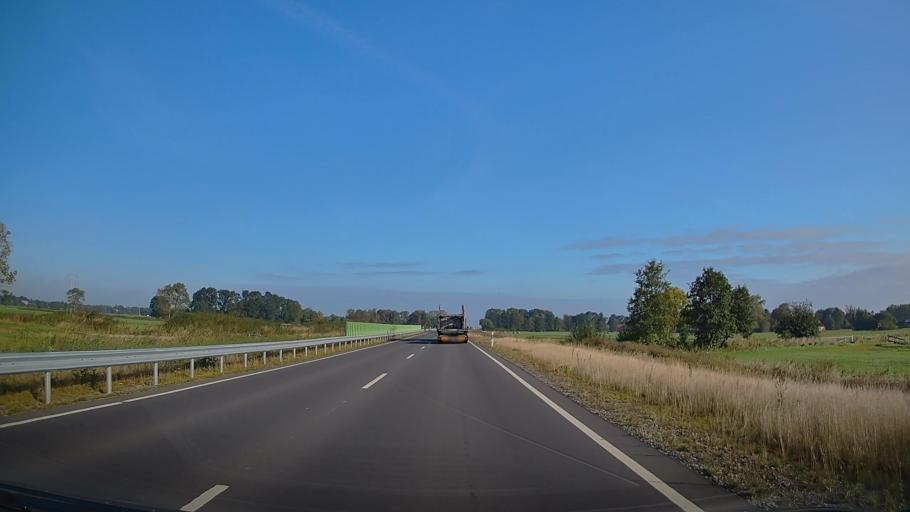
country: DE
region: Lower Saxony
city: Ovelgonne
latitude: 53.3036
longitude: 8.3971
